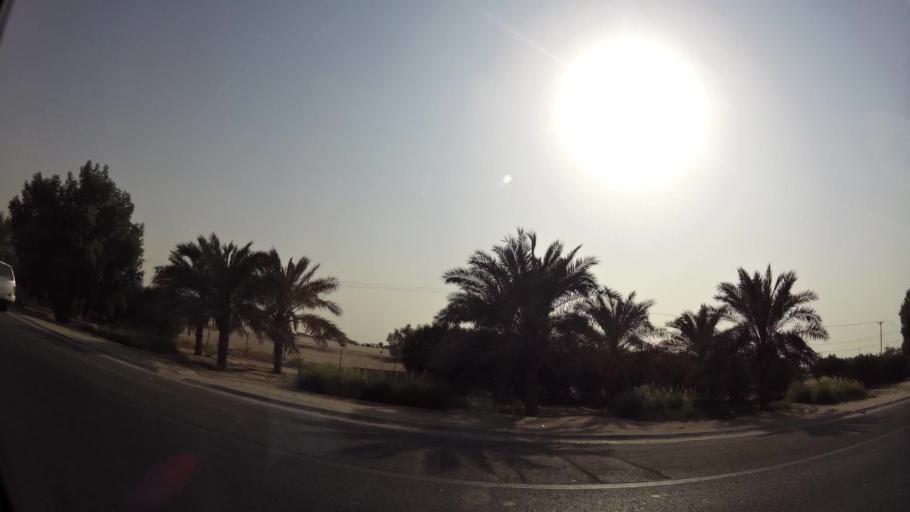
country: KW
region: Muhafazat al Jahra'
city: Al Jahra'
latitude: 29.3157
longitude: 47.7678
